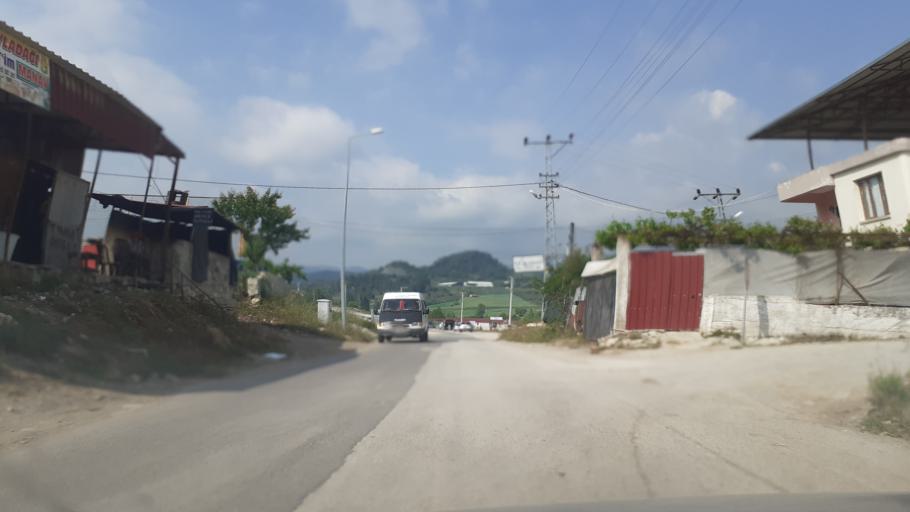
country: TR
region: Hatay
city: Yayladagi
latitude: 35.9088
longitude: 36.0533
